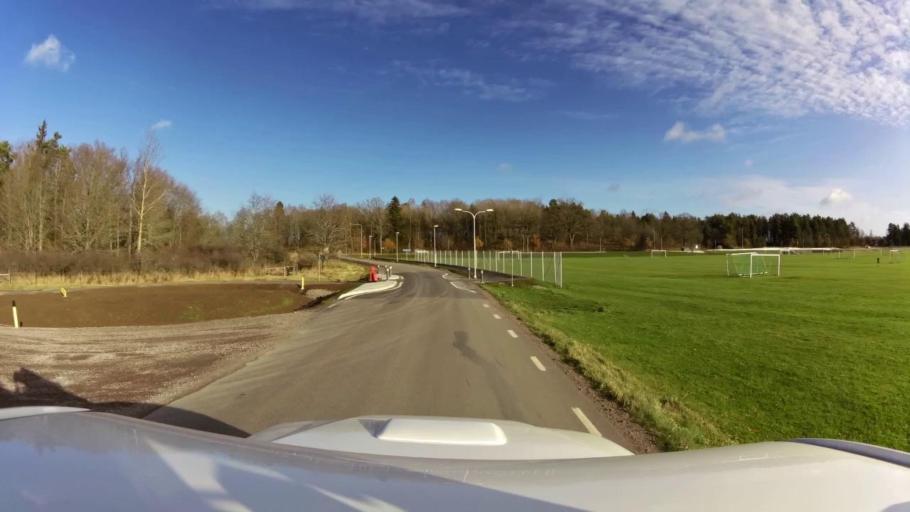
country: SE
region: OEstergoetland
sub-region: Linkopings Kommun
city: Linkoping
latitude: 58.3816
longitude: 15.6297
